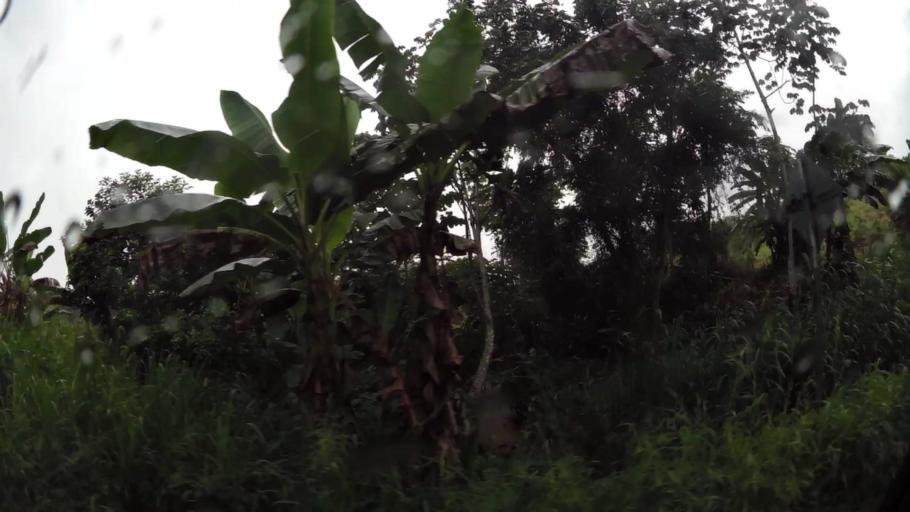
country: PA
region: Panama
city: Cabra Numero Uno
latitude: 9.1016
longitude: -79.3340
